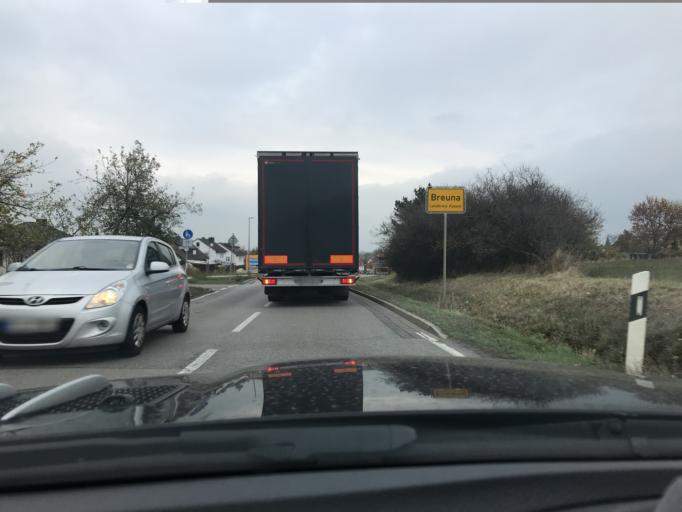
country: DE
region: Hesse
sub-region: Regierungsbezirk Kassel
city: Breuna
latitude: 51.4089
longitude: 9.1831
